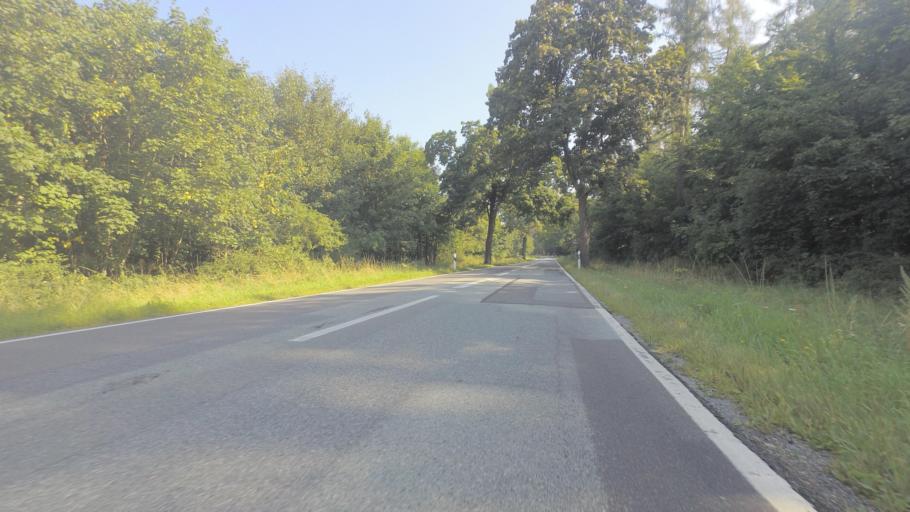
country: DE
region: Mecklenburg-Vorpommern
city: Malchow
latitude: 53.5860
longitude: 12.4686
